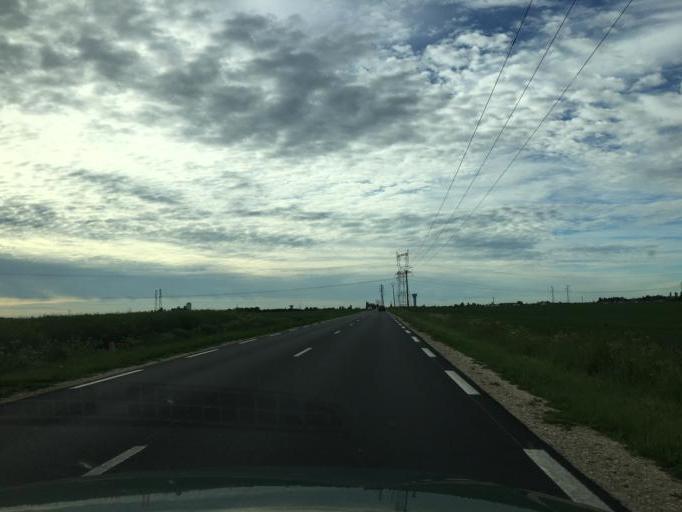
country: FR
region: Centre
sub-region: Departement du Loiret
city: Ormes
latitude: 47.9525
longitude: 1.8017
